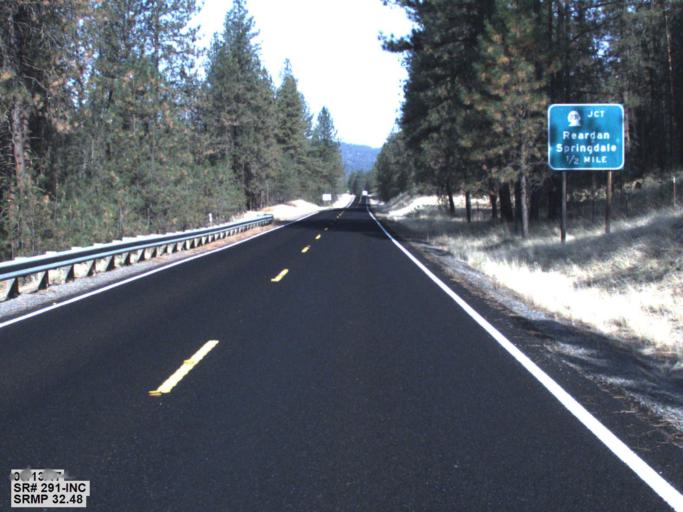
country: US
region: Washington
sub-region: Spokane County
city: Fairchild Air Force Base
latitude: 47.8424
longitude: -117.8462
